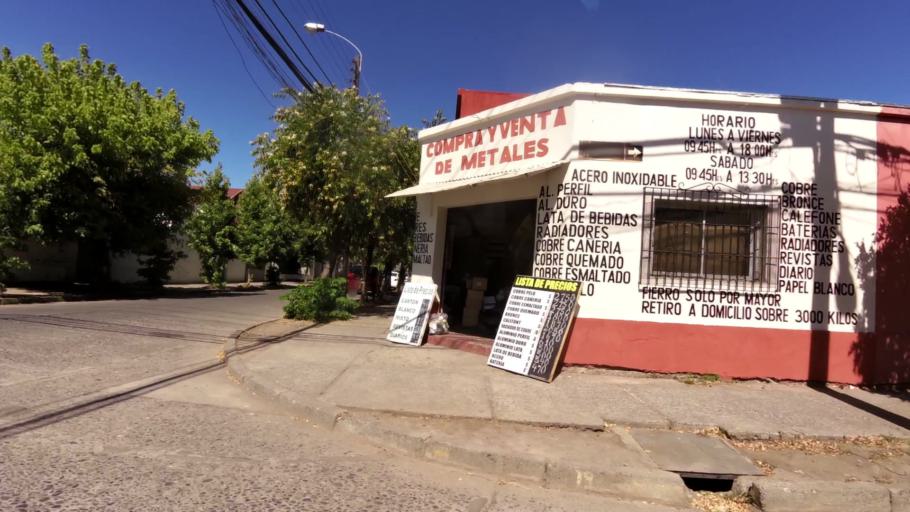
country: CL
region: O'Higgins
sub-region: Provincia de Colchagua
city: Chimbarongo
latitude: -34.5873
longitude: -70.9942
